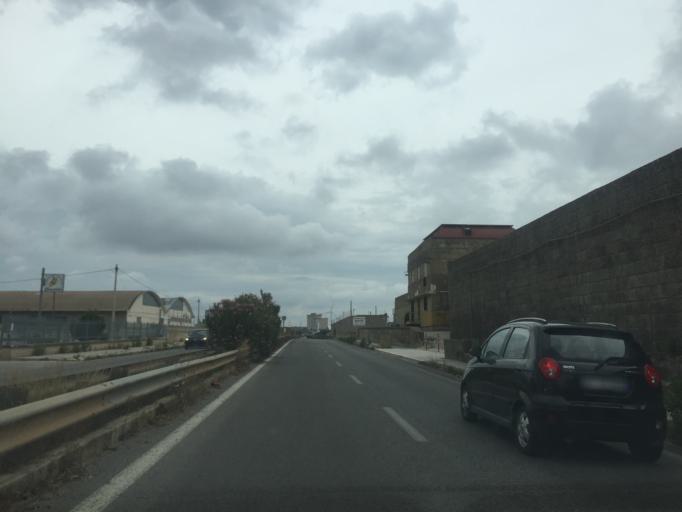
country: IT
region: Sicily
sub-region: Ragusa
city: Ragusa
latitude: 36.8859
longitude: 14.6863
